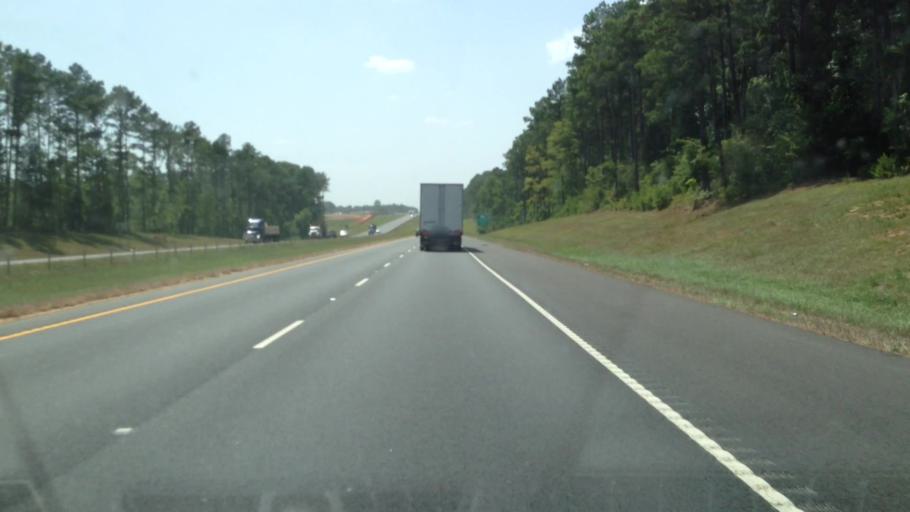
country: US
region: Louisiana
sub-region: Webster Parish
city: Minden
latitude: 32.5773
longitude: -93.2321
